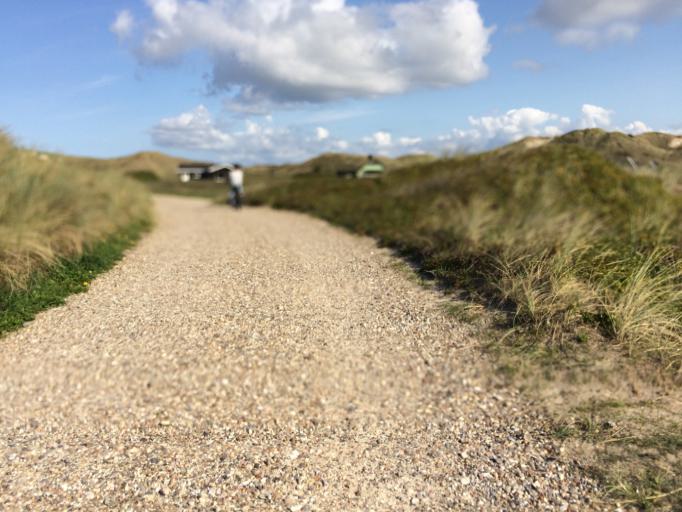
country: DK
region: Central Jutland
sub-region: Ringkobing-Skjern Kommune
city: Hvide Sande
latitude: 55.9279
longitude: 8.1512
